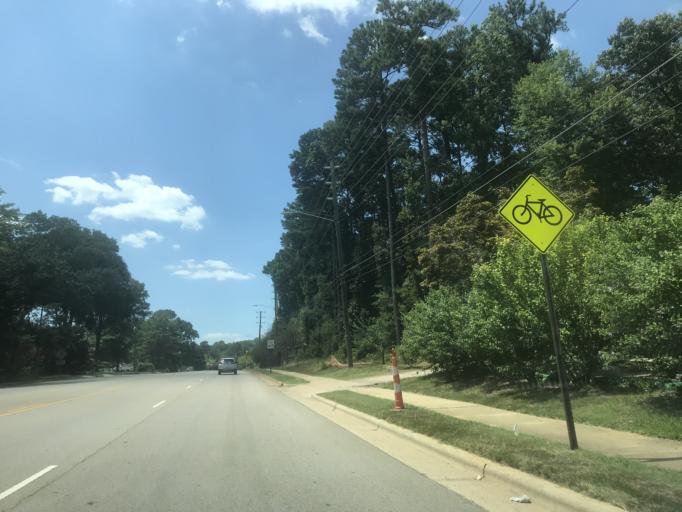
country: US
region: North Carolina
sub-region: Wake County
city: Cary
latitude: 35.7655
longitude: -78.7538
